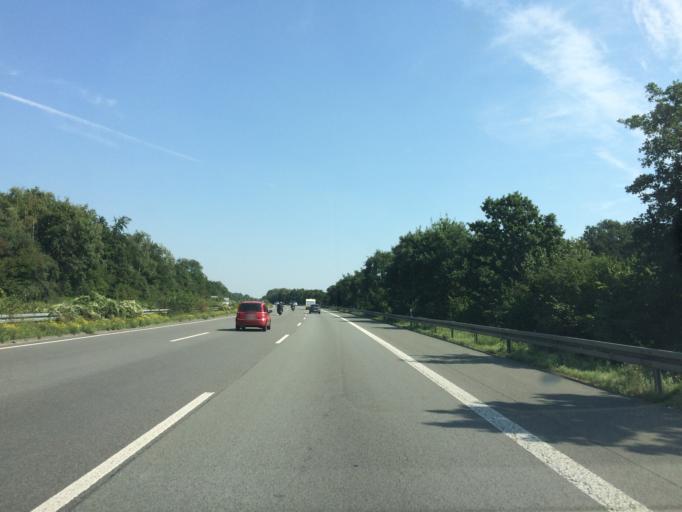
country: DE
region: North Rhine-Westphalia
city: Oer-Erkenschwick
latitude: 51.5996
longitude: 7.2874
